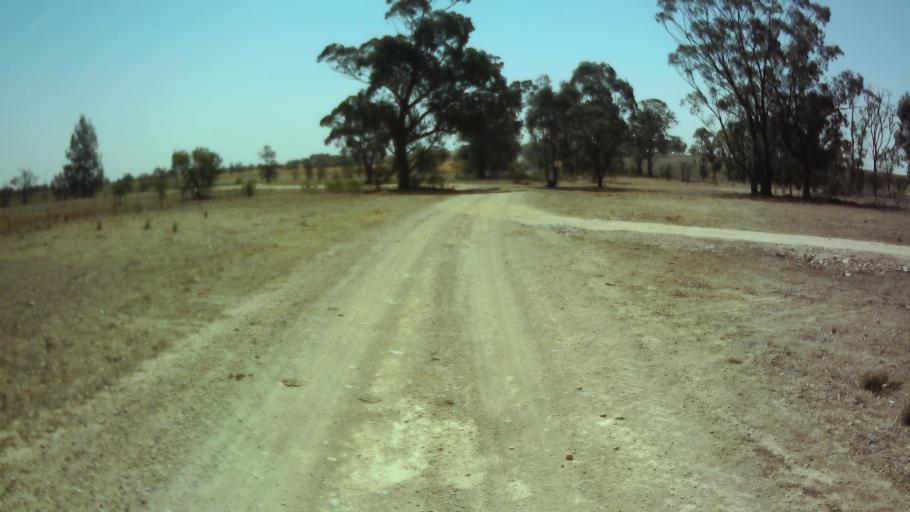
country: AU
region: New South Wales
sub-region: Weddin
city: Grenfell
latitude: -33.9103
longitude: 147.7669
